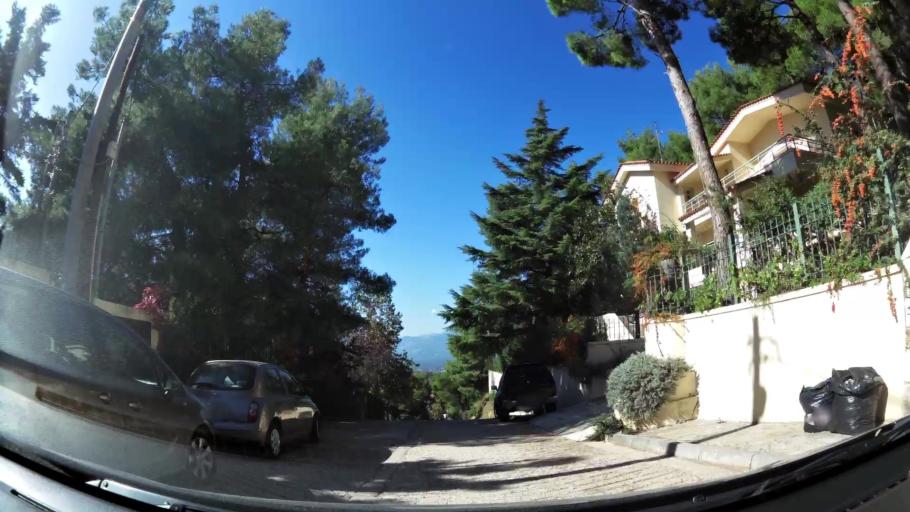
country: GR
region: Attica
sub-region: Nomarchia Anatolikis Attikis
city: Dionysos
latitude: 38.1075
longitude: 23.8891
